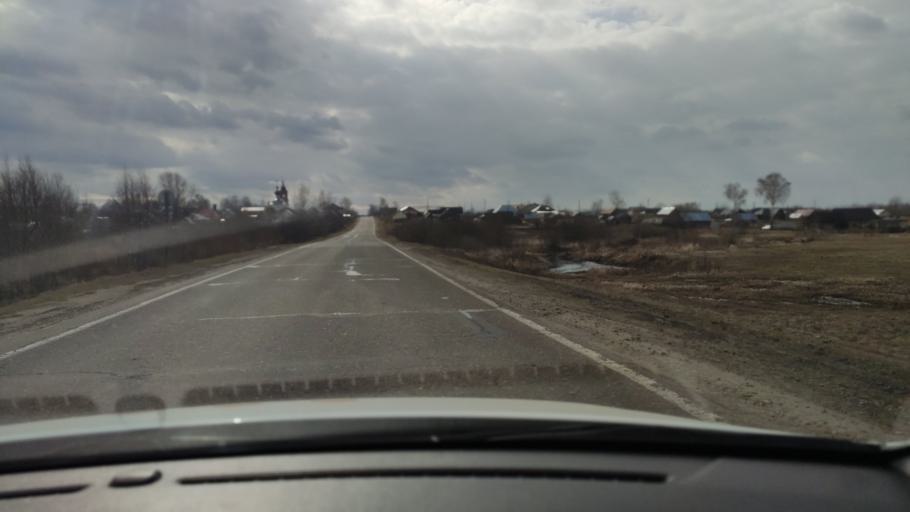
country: RU
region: Tatarstan
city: Vysokaya Gora
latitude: 56.1948
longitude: 49.2104
